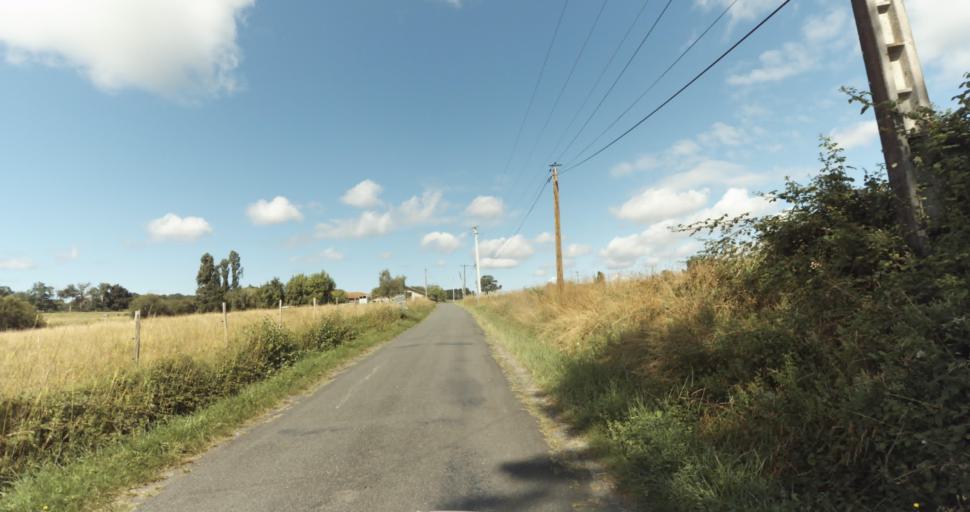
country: FR
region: Aquitaine
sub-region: Departement de la Gironde
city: Bazas
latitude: 44.4507
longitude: -0.2070
